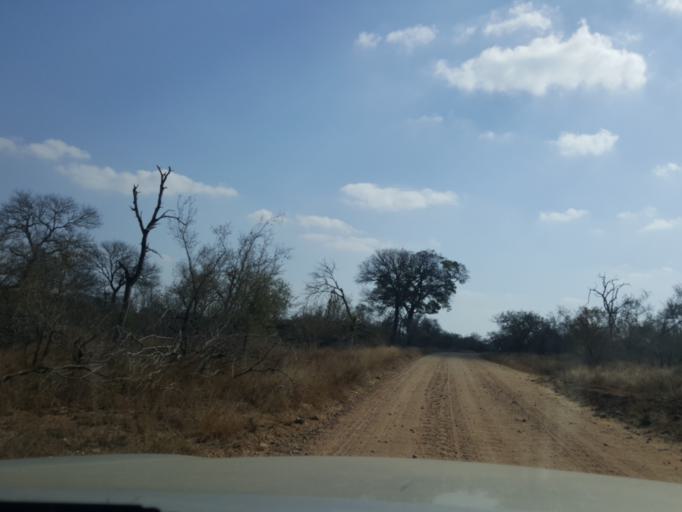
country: ZA
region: Mpumalanga
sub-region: Ehlanzeni District
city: Komatipoort
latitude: -25.2700
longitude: 31.8019
